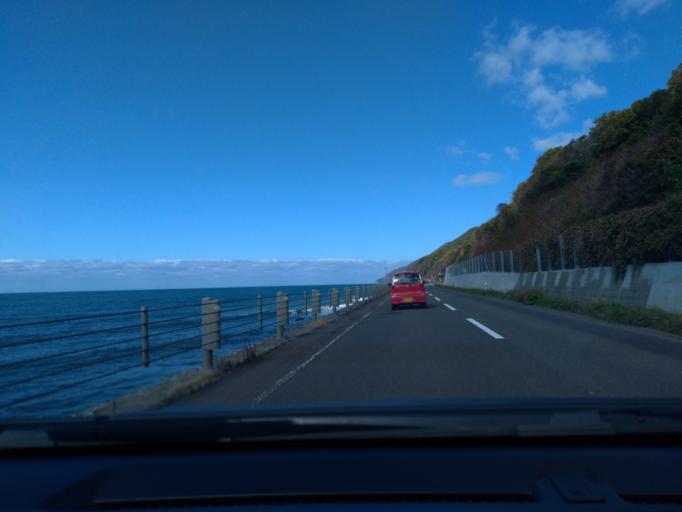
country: JP
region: Hokkaido
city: Ishikari
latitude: 43.4281
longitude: 141.4222
